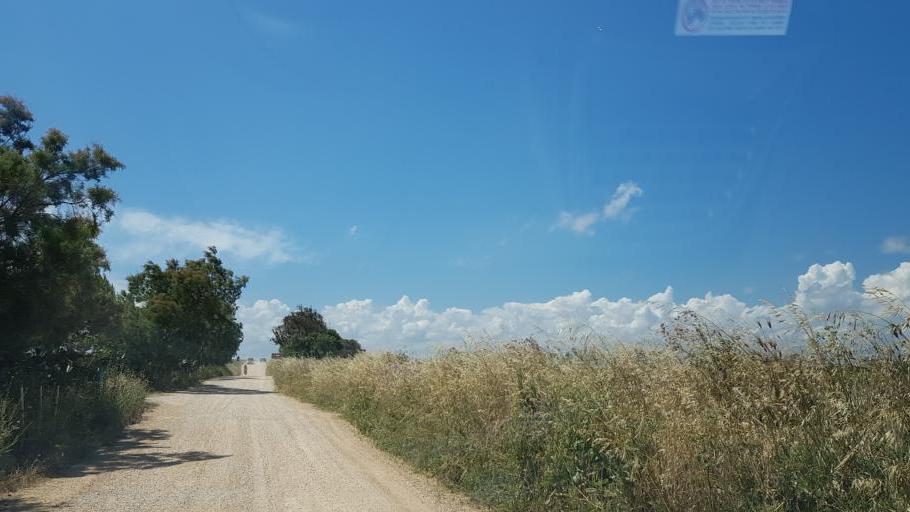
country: IT
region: Apulia
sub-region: Provincia di Brindisi
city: San Vito dei Normanni
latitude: 40.6969
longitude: 17.8199
